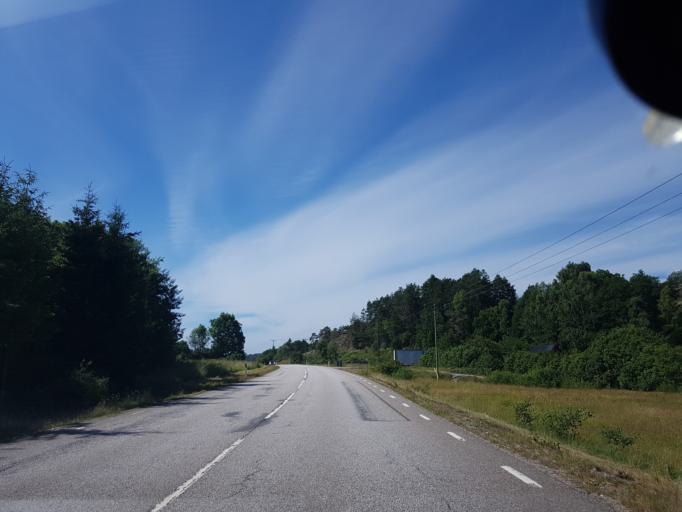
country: SE
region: Vaestra Goetaland
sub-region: Lysekils Kommun
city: Lysekil
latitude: 58.1612
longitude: 11.4751
